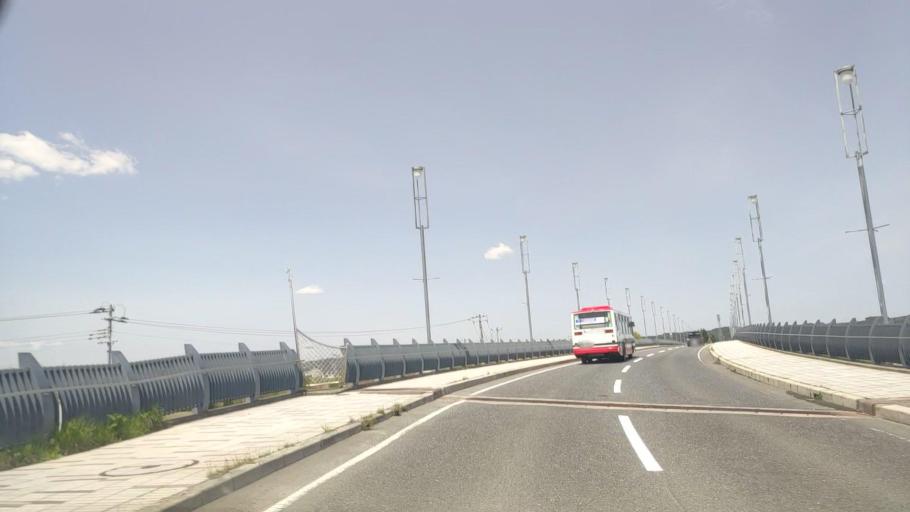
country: JP
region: Aomori
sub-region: Hachinohe Shi
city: Uchimaru
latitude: 40.4999
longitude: 141.4441
